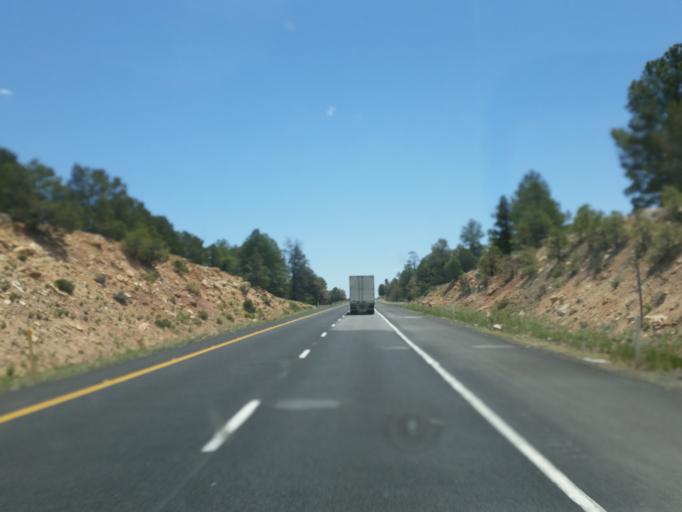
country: US
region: Arizona
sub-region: Coconino County
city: Flagstaff
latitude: 35.2138
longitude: -111.5407
